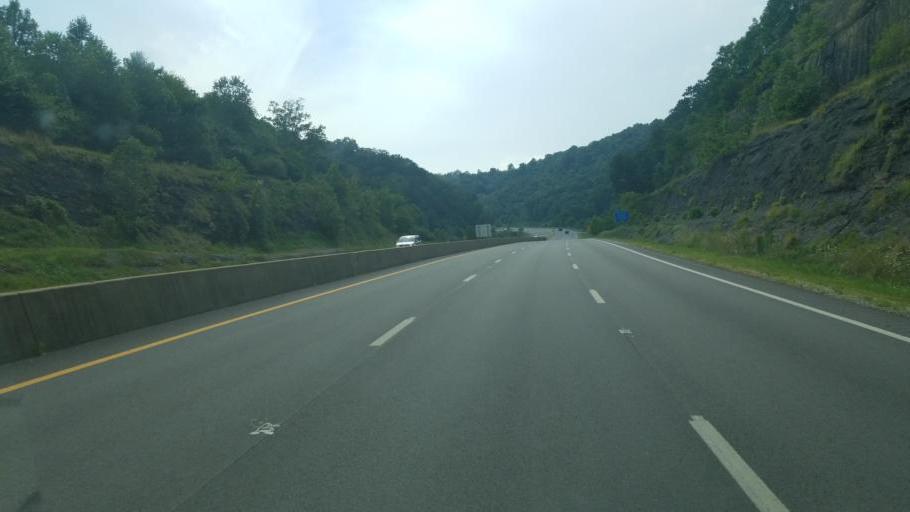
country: US
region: West Virginia
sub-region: Logan County
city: Chapmanville
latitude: 37.9274
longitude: -82.0202
